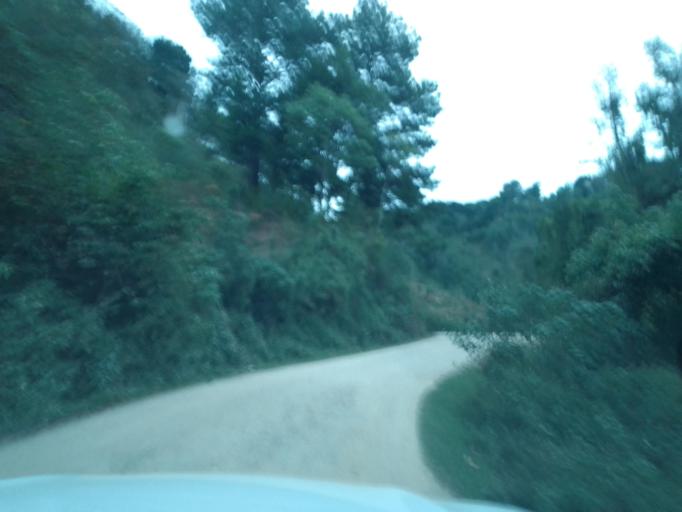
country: MX
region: Chiapas
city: Motozintla de Mendoza
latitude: 15.2160
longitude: -92.2383
